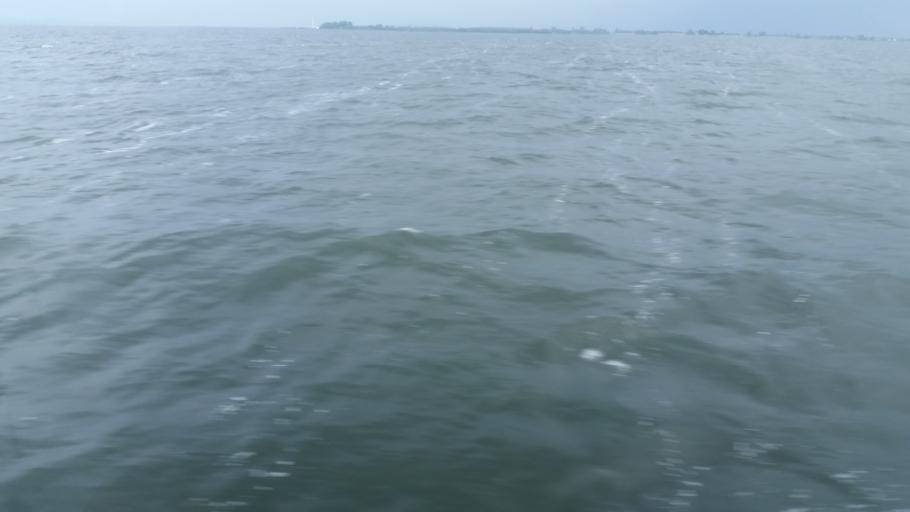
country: DE
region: Mecklenburg-Vorpommern
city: Hiddensee
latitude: 54.5250
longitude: 13.1335
